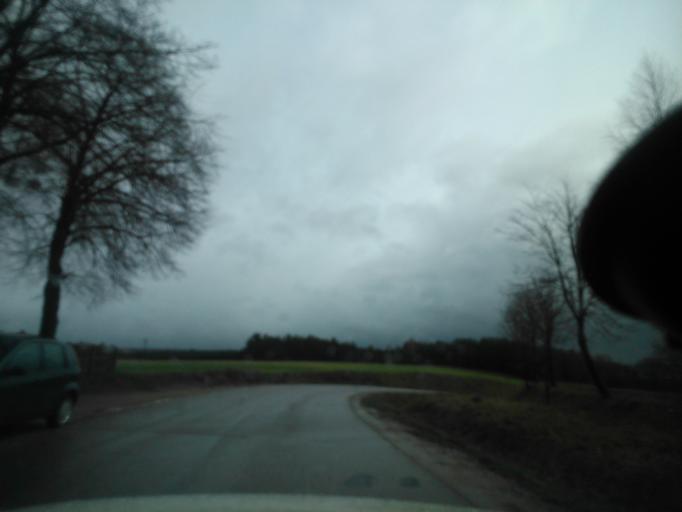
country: PL
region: Warmian-Masurian Voivodeship
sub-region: Powiat dzialdowski
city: Lidzbark
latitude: 53.3064
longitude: 19.8637
